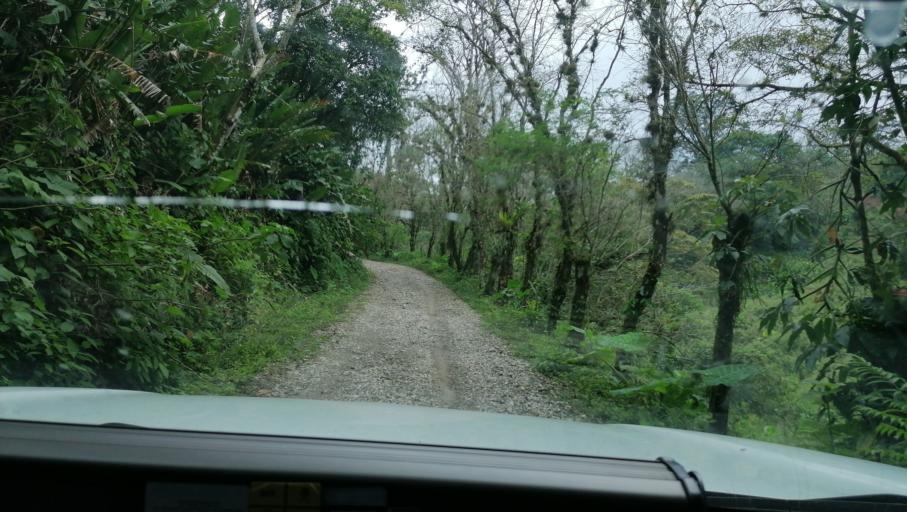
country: MX
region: Chiapas
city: Ixtacomitan
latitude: 17.3534
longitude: -93.1475
